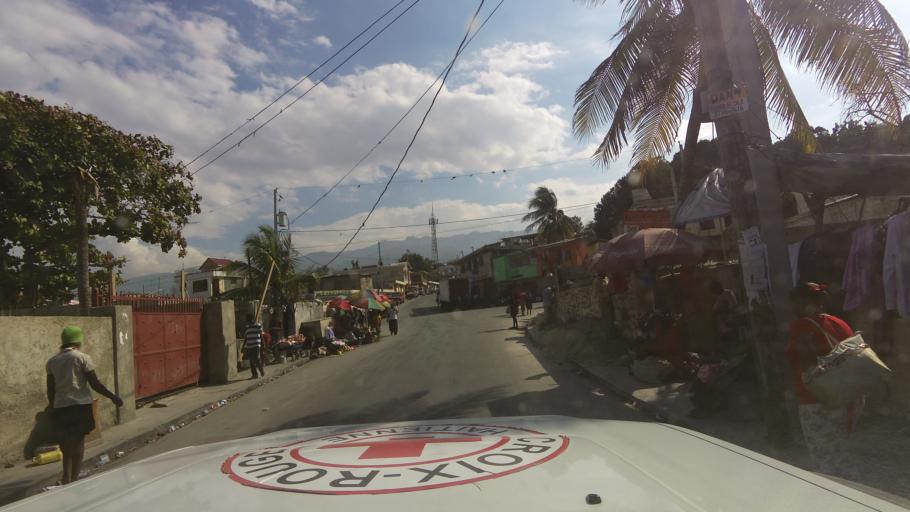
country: HT
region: Ouest
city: Petionville
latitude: 18.5275
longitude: -72.2820
